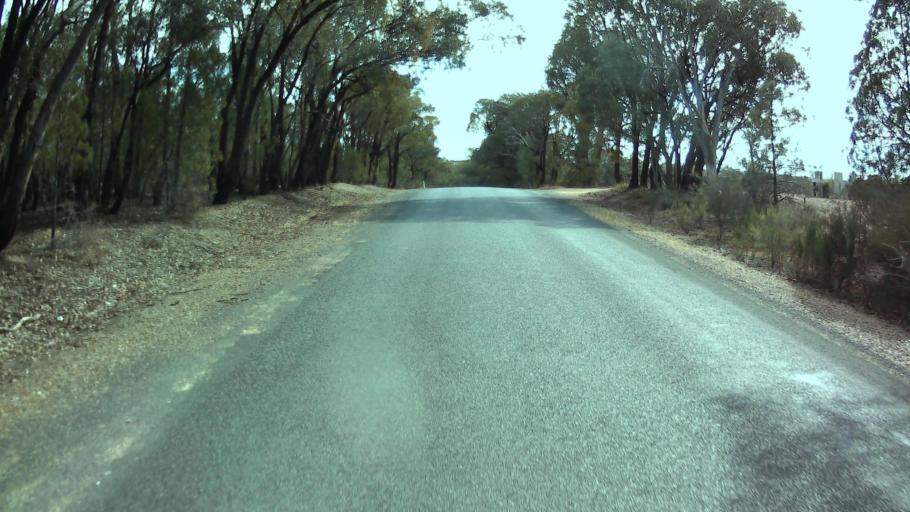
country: AU
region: New South Wales
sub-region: Weddin
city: Grenfell
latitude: -33.8918
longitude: 148.1914
